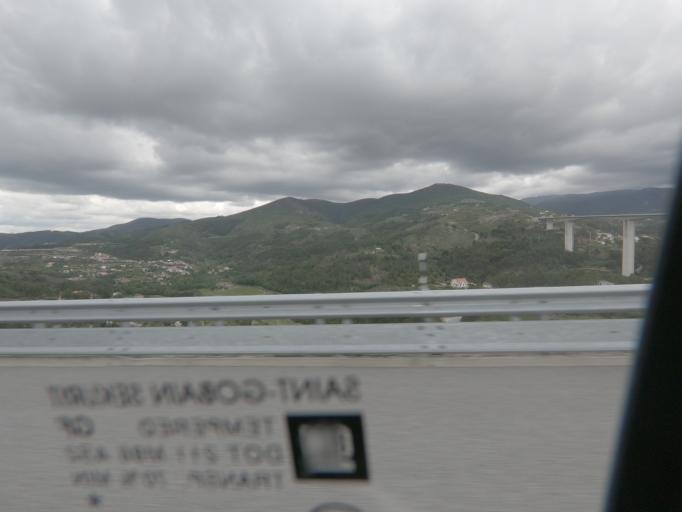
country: PT
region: Porto
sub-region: Amarante
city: Amarante
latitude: 41.2514
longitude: -7.9947
